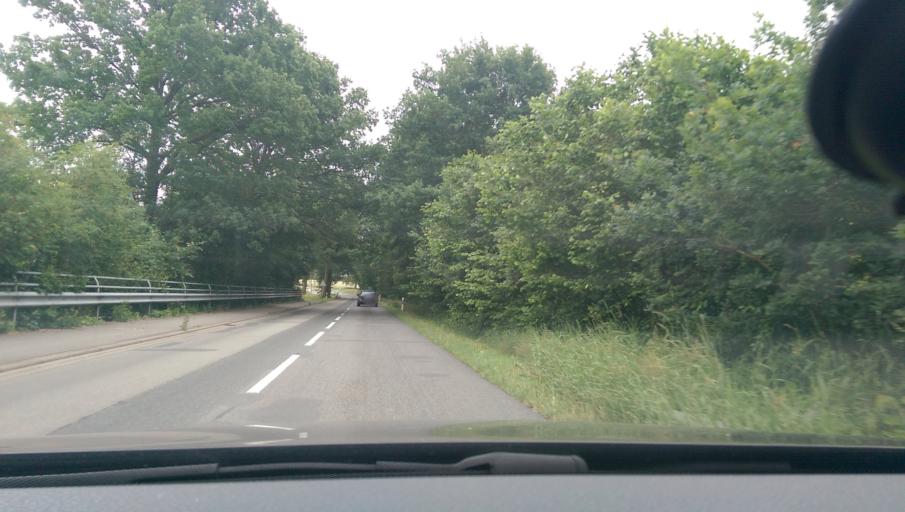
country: DE
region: Lower Saxony
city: Horstedt
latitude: 53.1768
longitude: 9.2647
